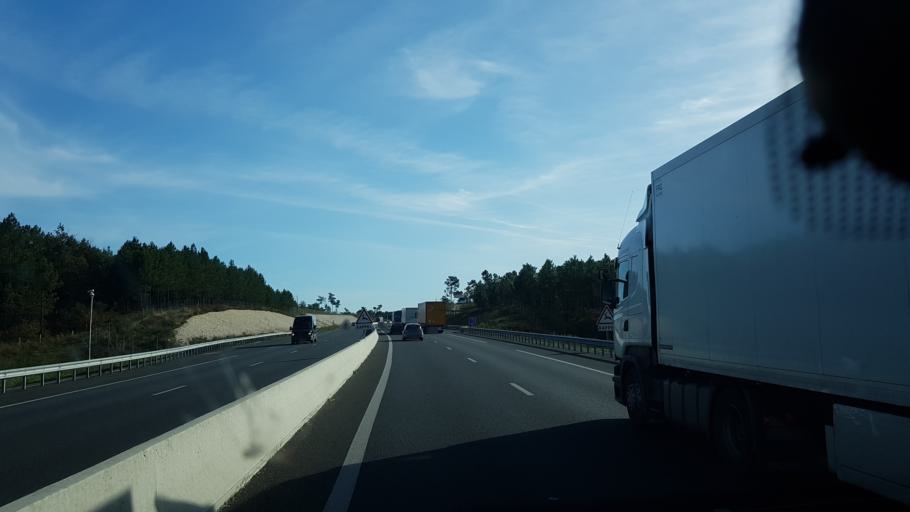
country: FR
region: Poitou-Charentes
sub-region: Departement de la Charente
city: Baignes-Sainte-Radegonde
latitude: 45.3785
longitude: -0.1818
